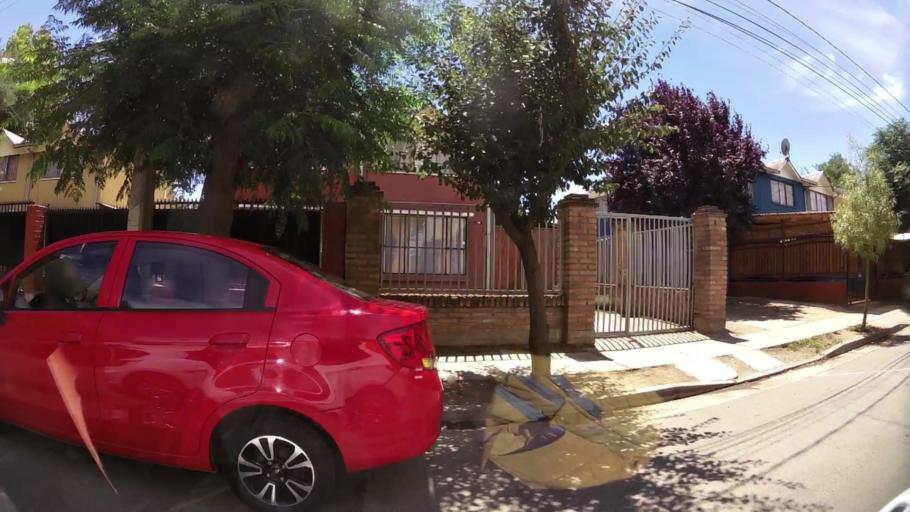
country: CL
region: O'Higgins
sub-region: Provincia de Cachapoal
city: Graneros
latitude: -34.0592
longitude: -70.7282
